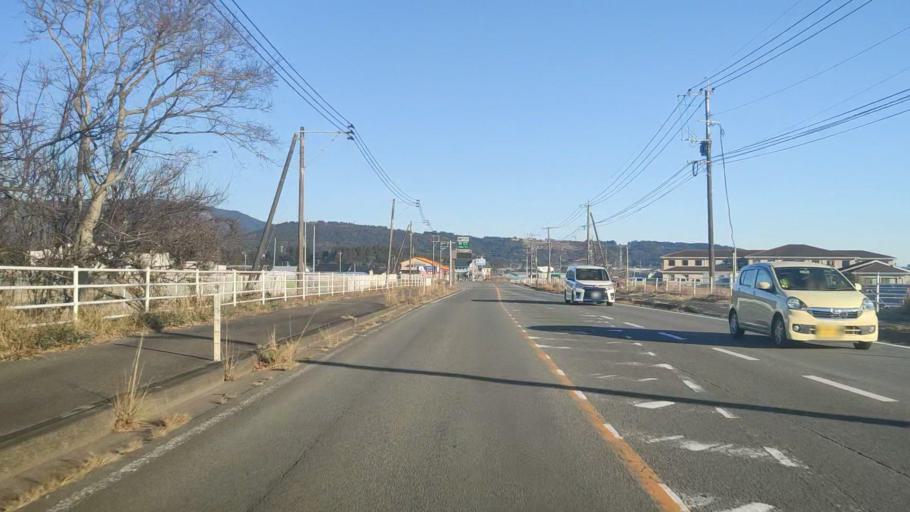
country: JP
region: Miyazaki
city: Takanabe
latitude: 32.2472
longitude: 131.5517
